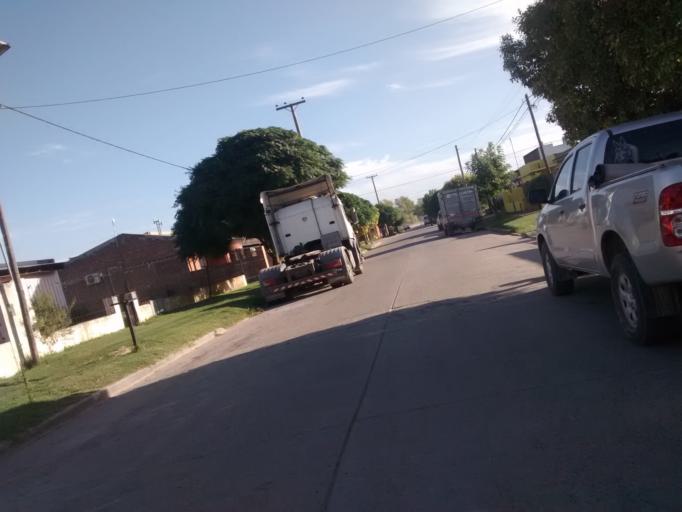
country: AR
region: Buenos Aires
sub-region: Partido de Loberia
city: Loberia
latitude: -38.1693
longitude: -58.7809
